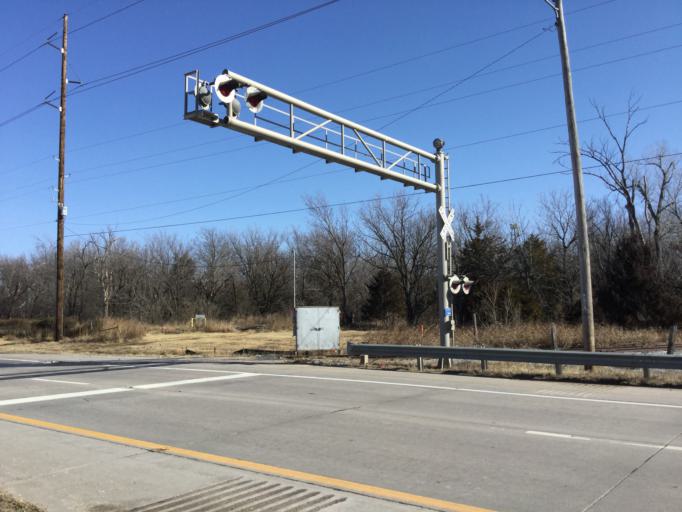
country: US
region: Kansas
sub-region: Sedgwick County
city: Derby
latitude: 37.6179
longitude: -97.2937
